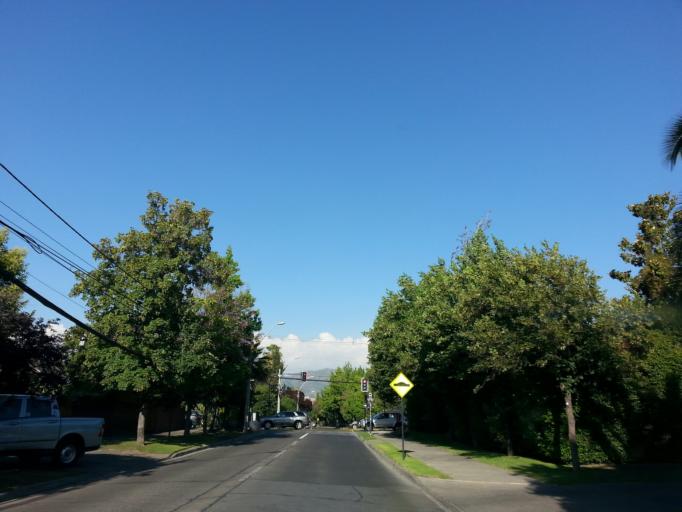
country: CL
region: Santiago Metropolitan
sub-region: Provincia de Santiago
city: Villa Presidente Frei, Nunoa, Santiago, Chile
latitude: -33.3847
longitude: -70.5435
